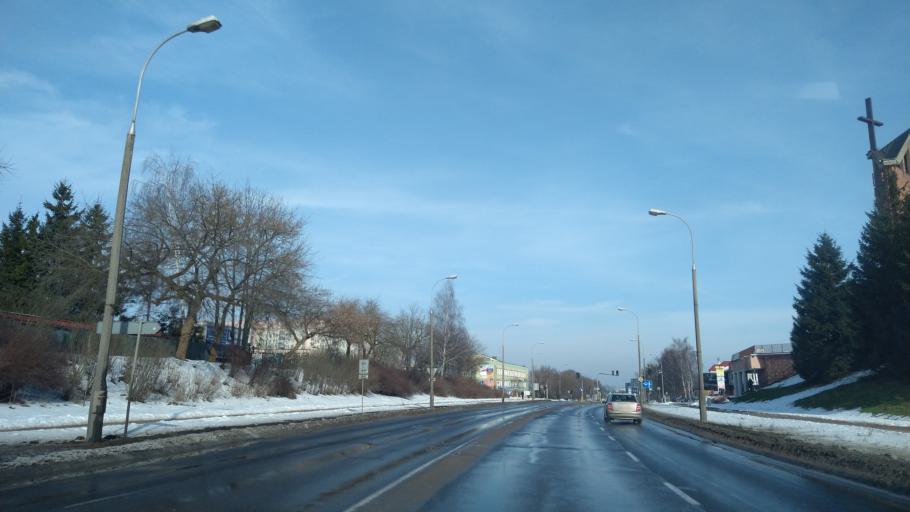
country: PL
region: Warmian-Masurian Voivodeship
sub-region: Powiat olsztynski
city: Olsztyn
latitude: 53.7648
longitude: 20.5026
